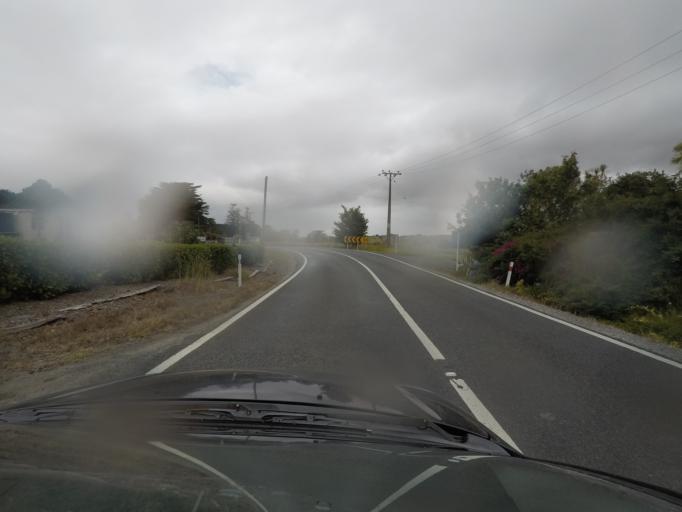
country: NZ
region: Auckland
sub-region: Auckland
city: Warkworth
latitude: -36.3372
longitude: 174.7017
